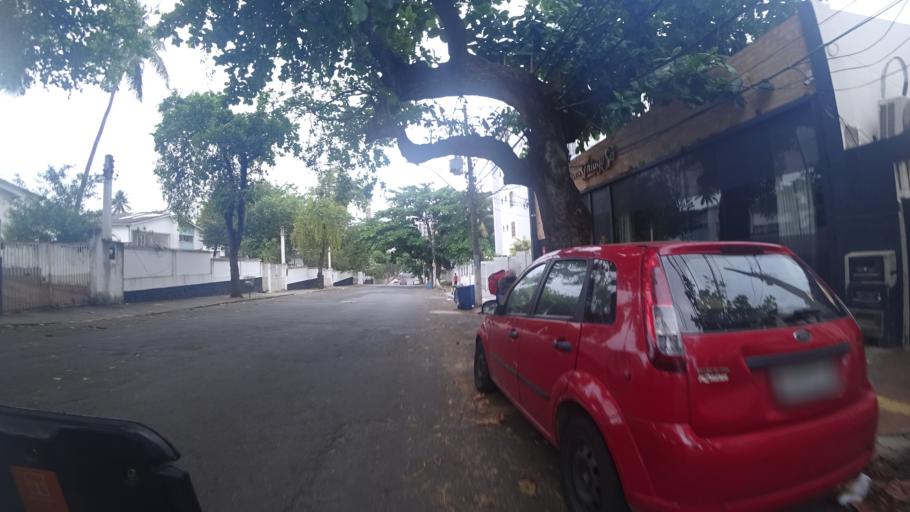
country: BR
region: Bahia
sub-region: Salvador
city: Salvador
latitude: -12.9995
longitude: -38.4586
